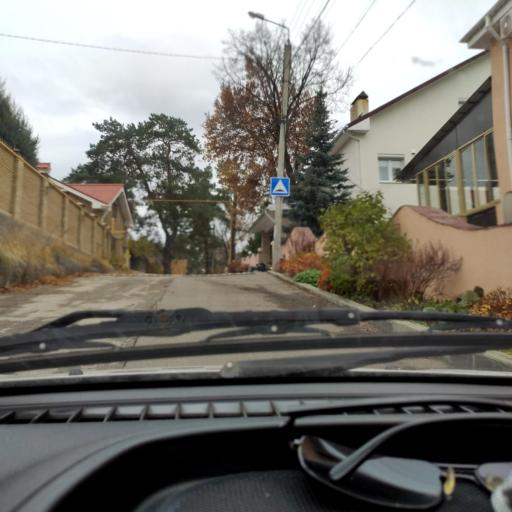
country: RU
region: Samara
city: Tol'yatti
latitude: 53.4806
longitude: 49.3553
